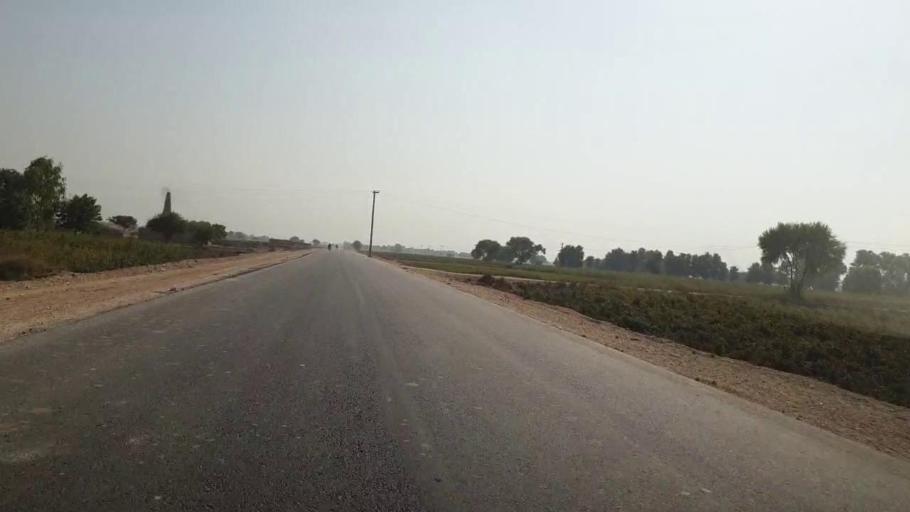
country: PK
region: Sindh
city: Dadu
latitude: 26.6620
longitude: 67.7764
